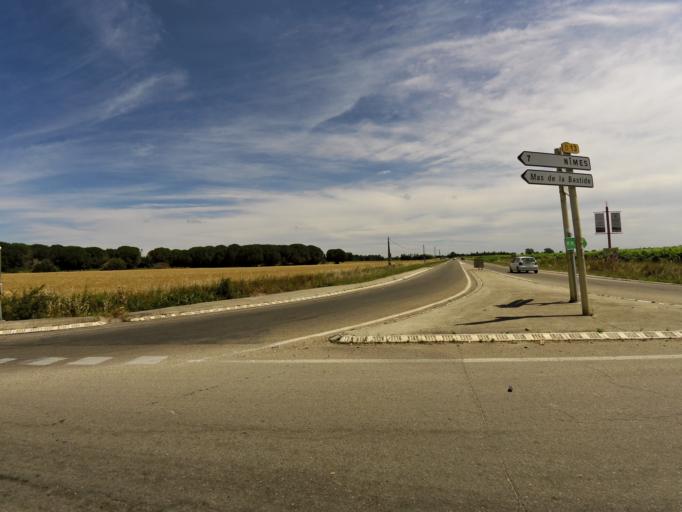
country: FR
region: Languedoc-Roussillon
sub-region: Departement du Gard
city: Caissargues
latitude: 43.7838
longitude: 4.3553
